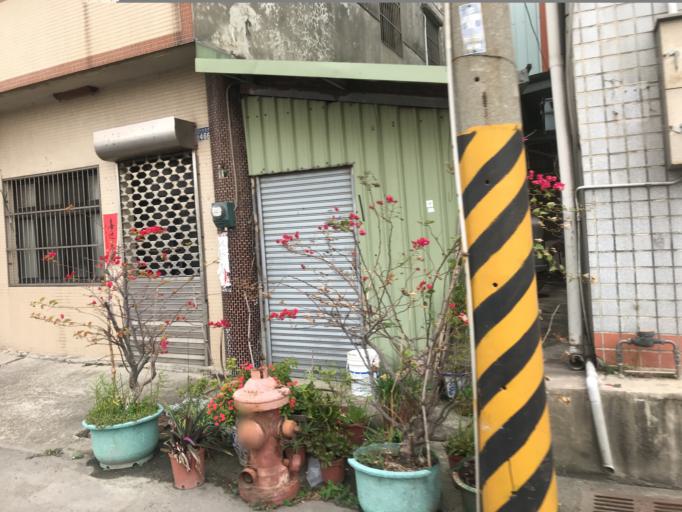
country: TW
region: Taiwan
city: Fengyuan
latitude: 24.3577
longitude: 120.6069
